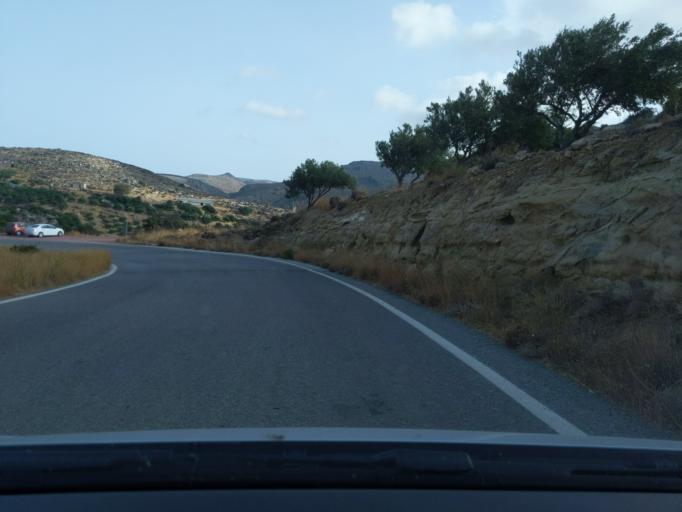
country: GR
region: Crete
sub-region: Nomos Lasithiou
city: Palekastro
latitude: 35.0962
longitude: 26.2354
